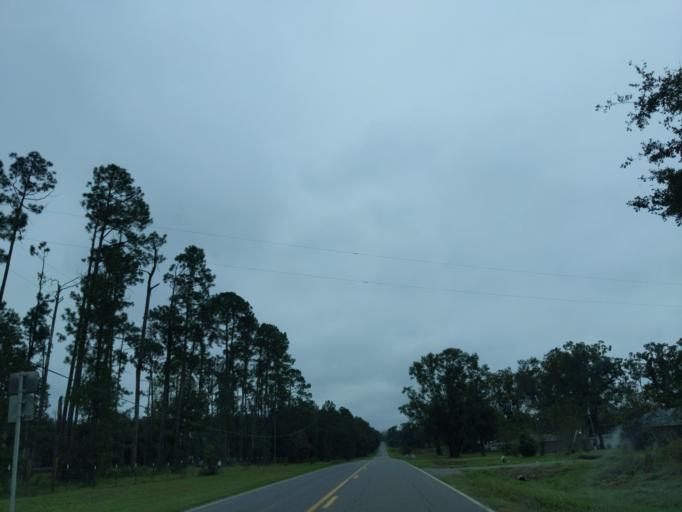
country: US
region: Florida
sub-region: Jackson County
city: Sneads
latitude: 30.7366
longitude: -84.9372
